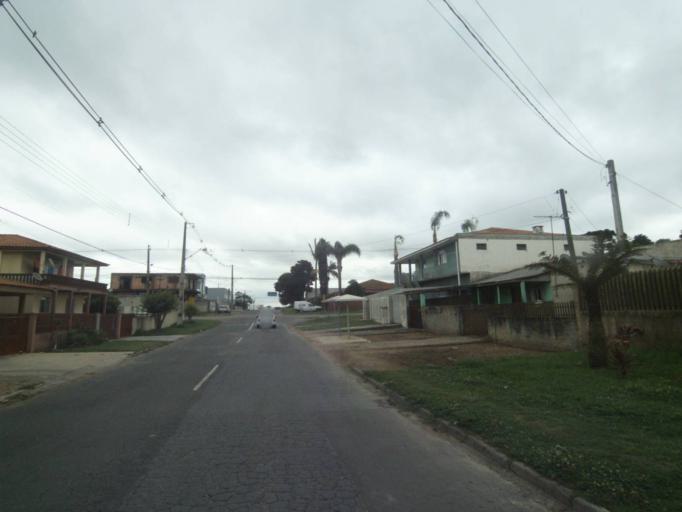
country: BR
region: Parana
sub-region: Sao Jose Dos Pinhais
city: Sao Jose dos Pinhais
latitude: -25.5514
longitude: -49.2758
